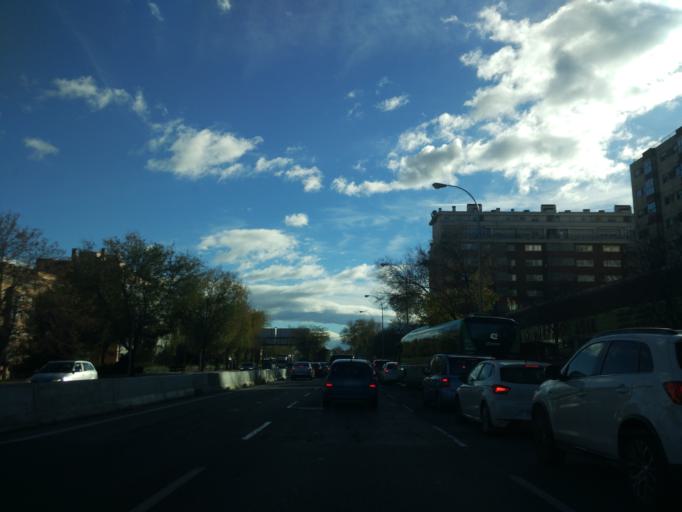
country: ES
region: Madrid
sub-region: Provincia de Madrid
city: Usera
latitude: 40.3735
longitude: -3.6949
